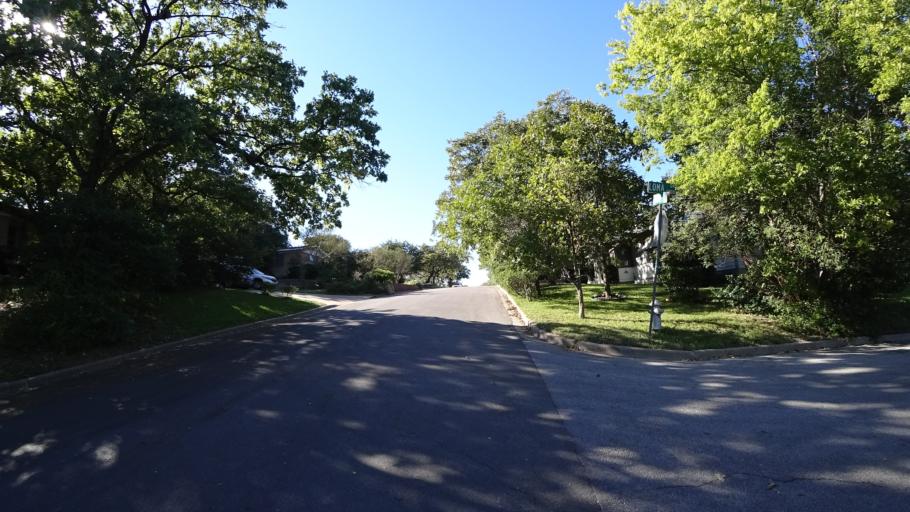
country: US
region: Texas
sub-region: Travis County
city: Austin
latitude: 30.2435
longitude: -97.7314
